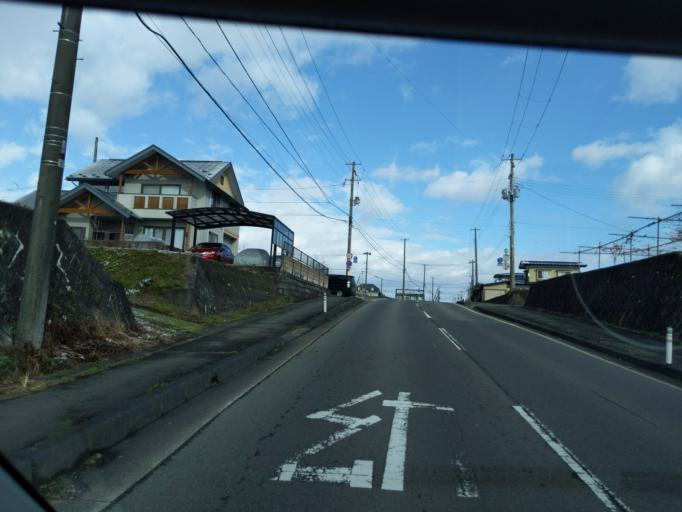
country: JP
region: Iwate
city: Mizusawa
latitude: 39.1099
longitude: 141.1363
